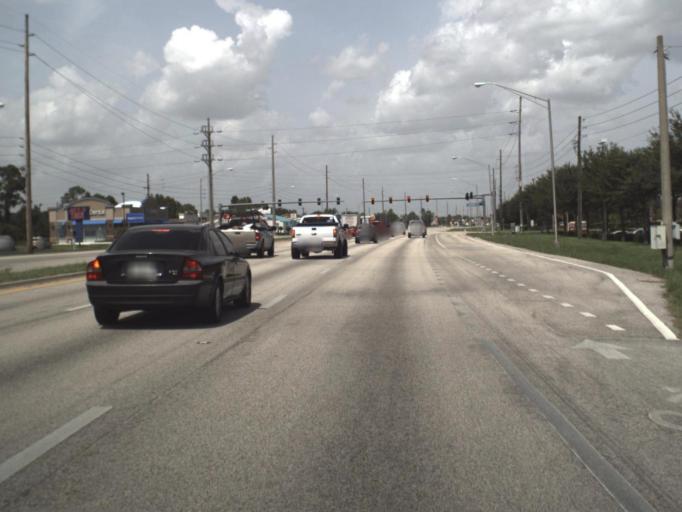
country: US
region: Florida
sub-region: Highlands County
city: Sebring
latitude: 27.4985
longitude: -81.4886
